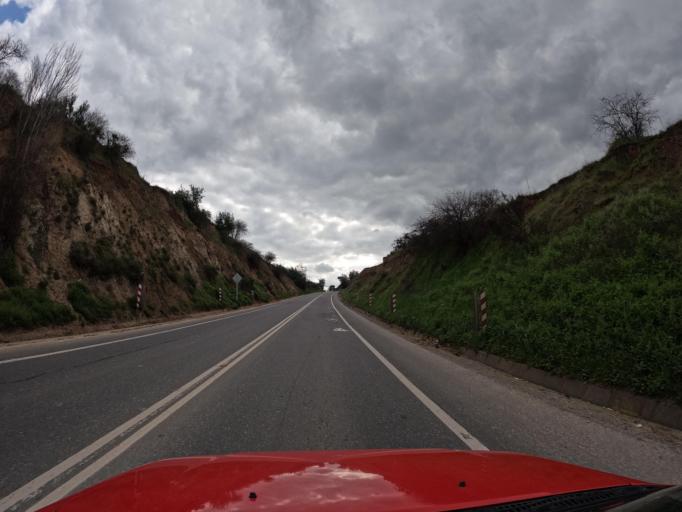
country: CL
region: Maule
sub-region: Provincia de Linares
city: San Javier
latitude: -35.6198
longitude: -71.7712
